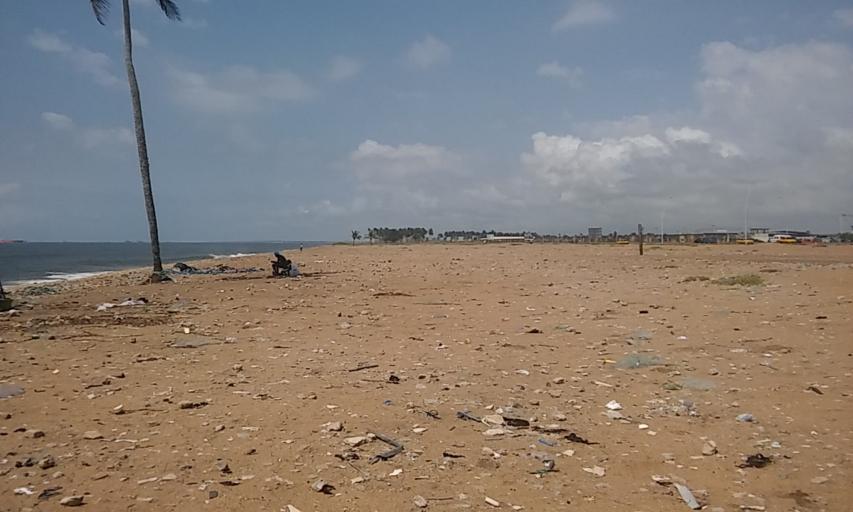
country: CI
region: Lagunes
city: Abidjan
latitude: 5.2436
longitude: -3.9285
